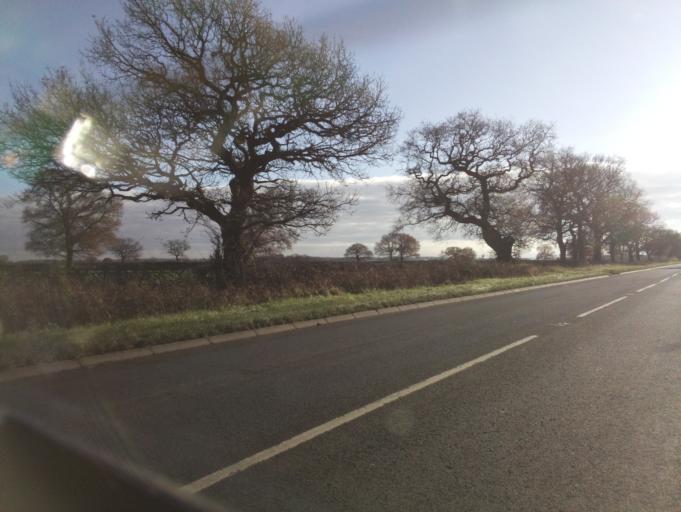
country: GB
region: England
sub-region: Staffordshire
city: Barton under Needwood
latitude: 52.8334
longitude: -1.7791
